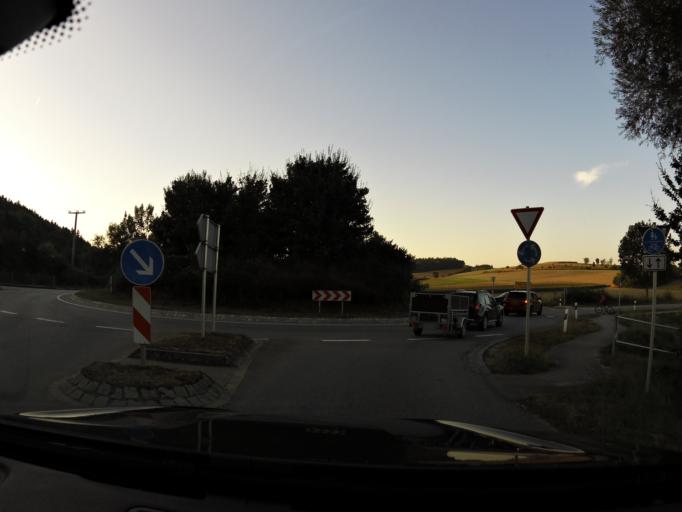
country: DE
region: Bavaria
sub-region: Lower Bavaria
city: Postau
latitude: 48.6447
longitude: 12.3152
